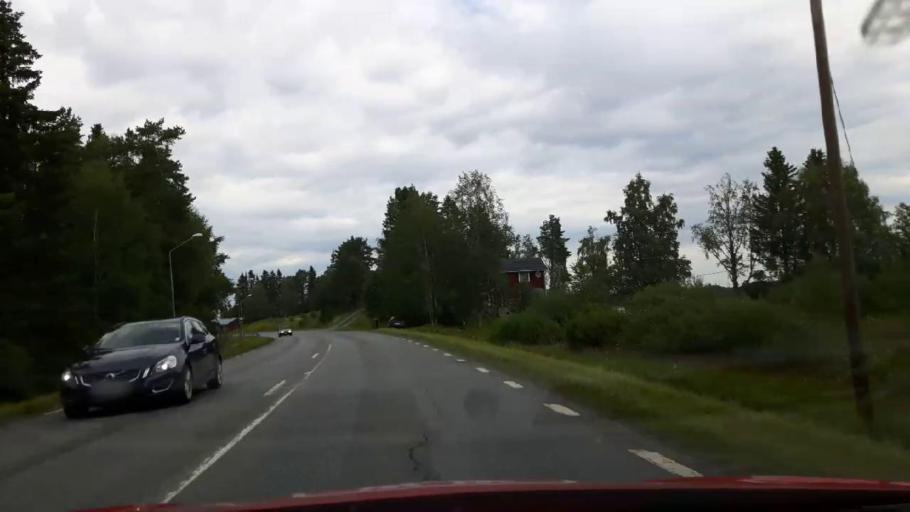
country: SE
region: Jaemtland
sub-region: Stroemsunds Kommun
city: Stroemsund
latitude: 63.5965
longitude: 15.3559
